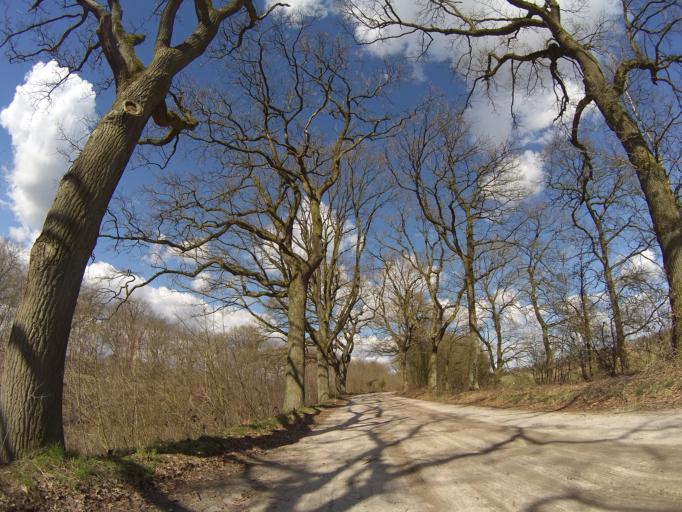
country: NL
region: Drenthe
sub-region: Gemeente Emmen
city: Emmen
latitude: 52.7781
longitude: 6.8739
